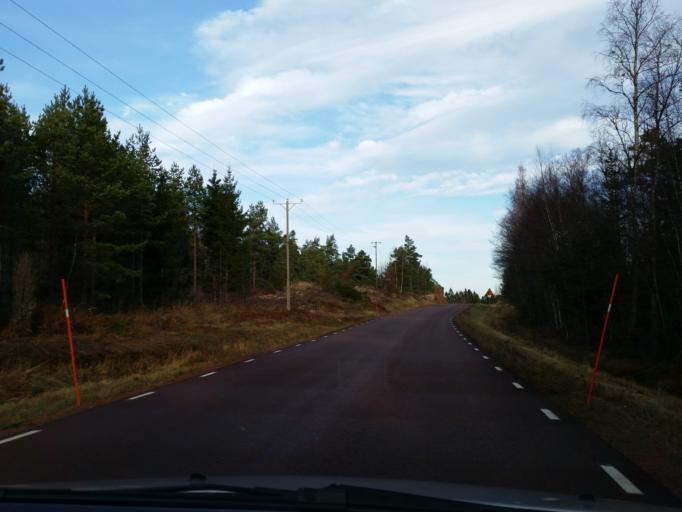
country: AX
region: Alands landsbygd
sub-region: Saltvik
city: Saltvik
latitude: 60.3384
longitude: 20.0964
